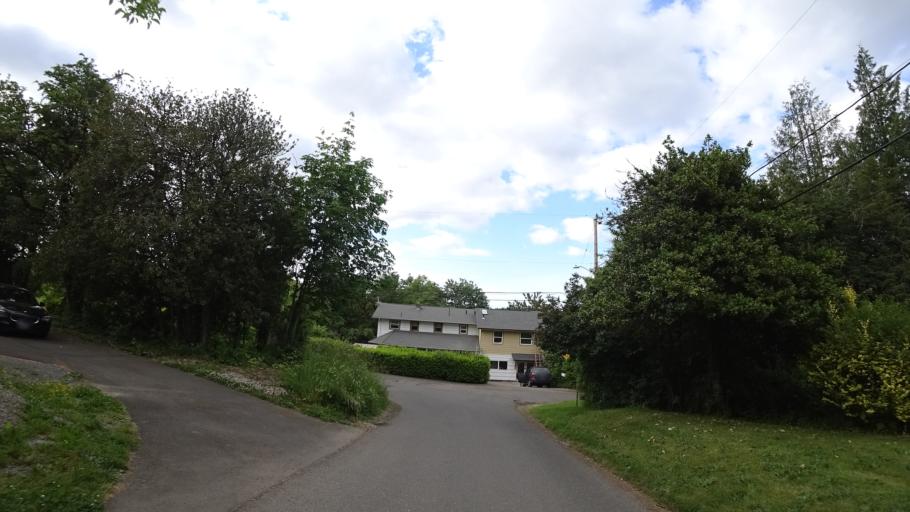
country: US
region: Oregon
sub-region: Washington County
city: Garden Home-Whitford
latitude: 45.4716
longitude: -122.7287
